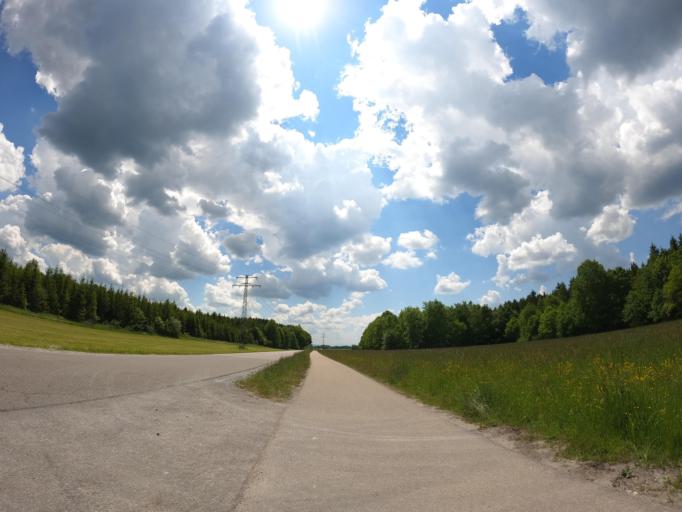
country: DE
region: Bavaria
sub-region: Upper Bavaria
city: Sauerlach
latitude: 47.9916
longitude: 11.6593
